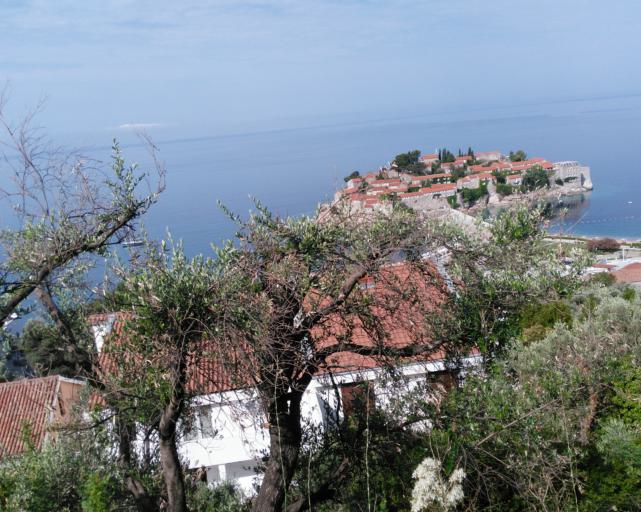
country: ME
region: Budva
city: Budva
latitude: 42.2572
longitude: 18.8965
